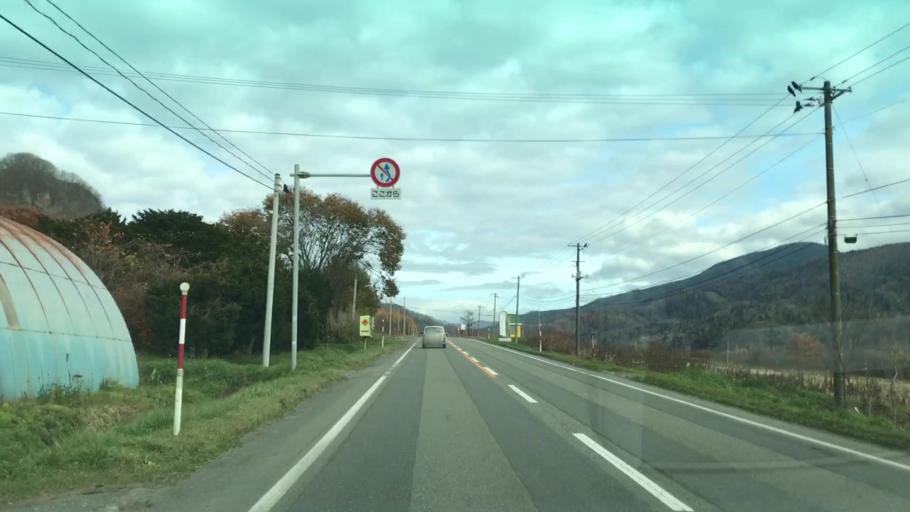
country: JP
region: Hokkaido
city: Shizunai-furukawacho
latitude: 42.7774
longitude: 142.3876
